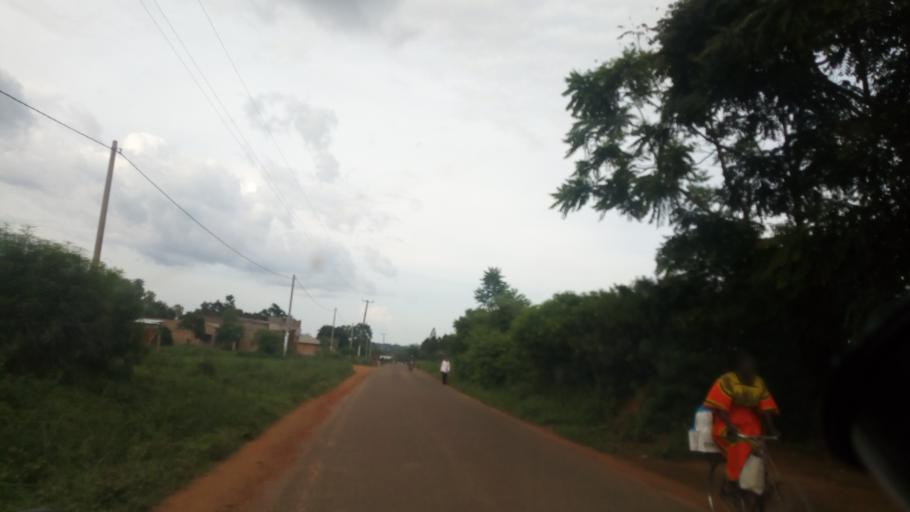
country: UG
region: Northern Region
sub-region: Lira District
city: Lira
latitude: 2.2565
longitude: 32.8495
